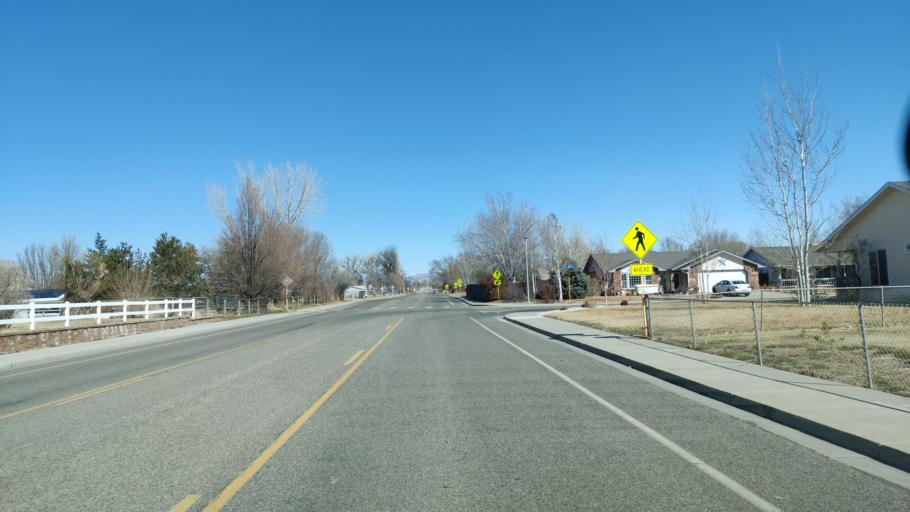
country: US
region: Colorado
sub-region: Mesa County
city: Fruita
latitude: 39.1671
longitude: -108.7197
